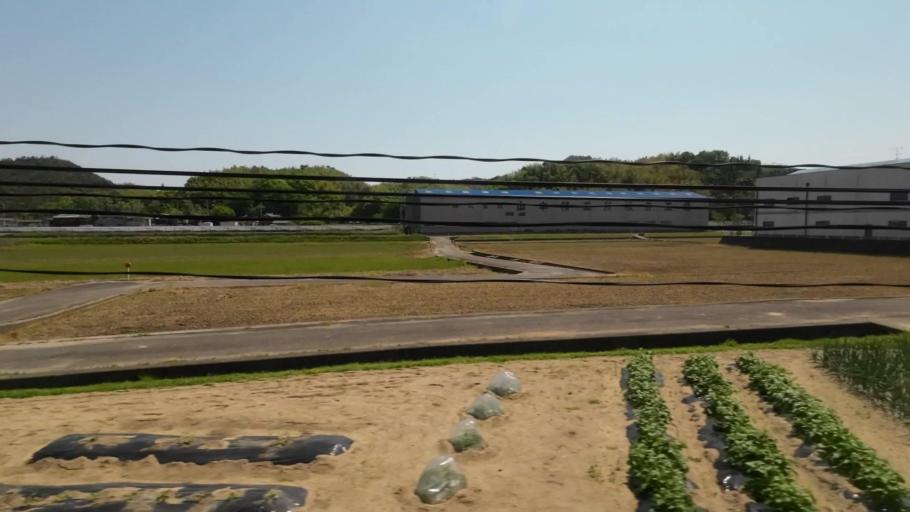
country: JP
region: Ehime
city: Saijo
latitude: 34.0051
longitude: 133.0361
